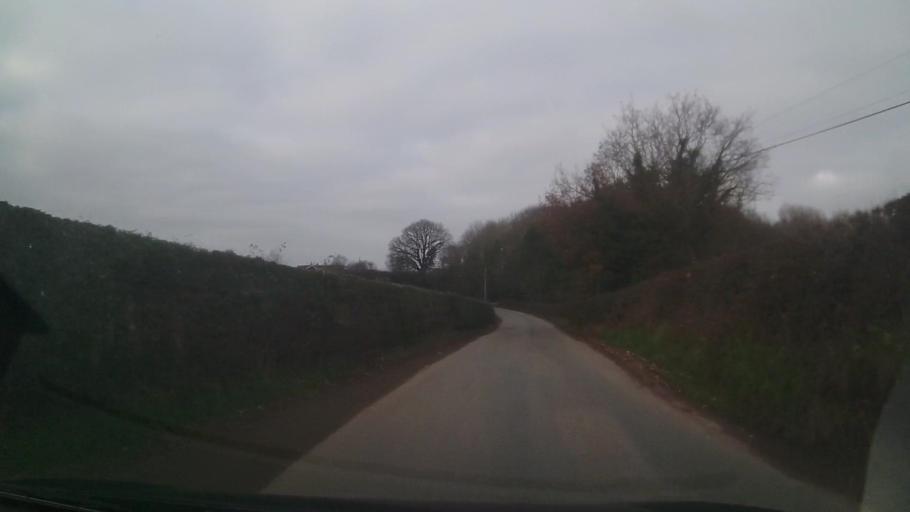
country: GB
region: England
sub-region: Shropshire
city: Bicton
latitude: 52.7718
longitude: -2.8431
